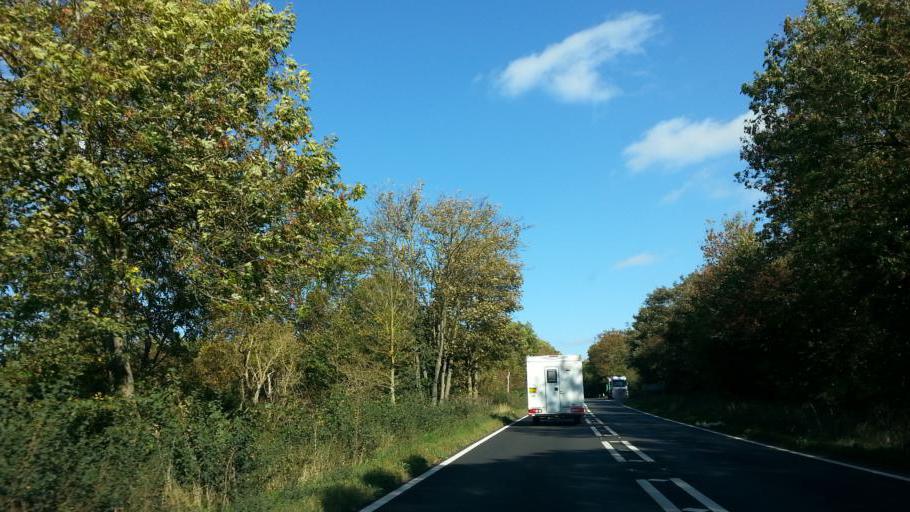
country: GB
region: England
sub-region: Northamptonshire
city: Oundle
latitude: 52.4383
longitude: -0.4750
